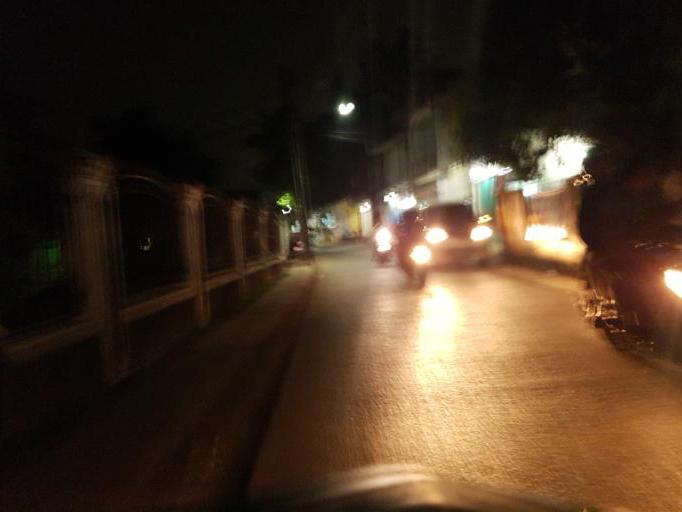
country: ID
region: West Java
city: Cileungsir
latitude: -6.3165
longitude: 106.9173
